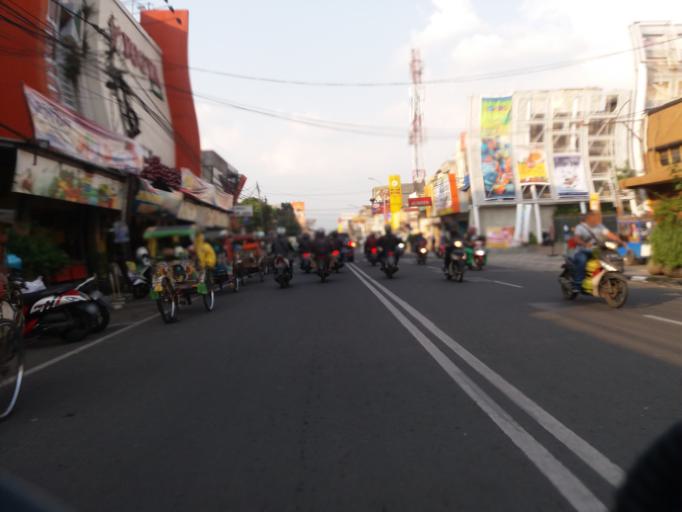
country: ID
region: West Java
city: Bandung
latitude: -6.9203
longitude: 107.6213
